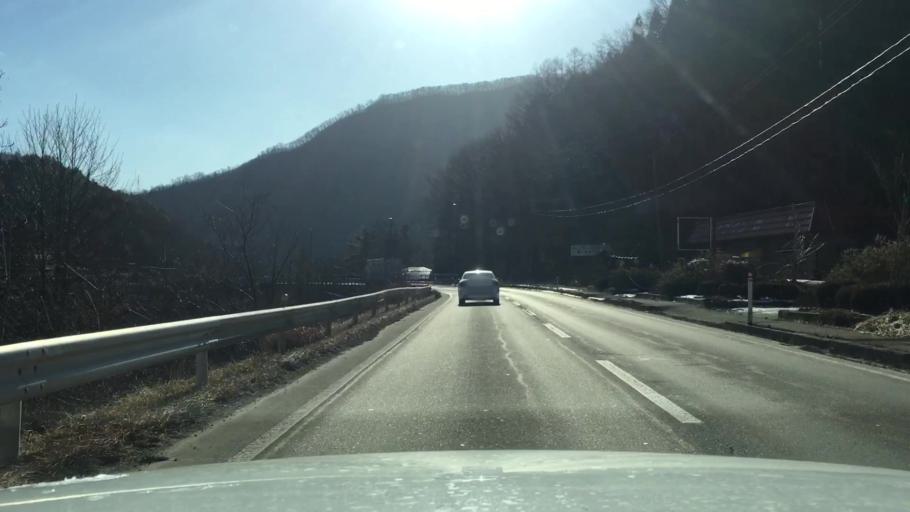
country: JP
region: Iwate
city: Tono
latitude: 39.6165
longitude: 141.6248
